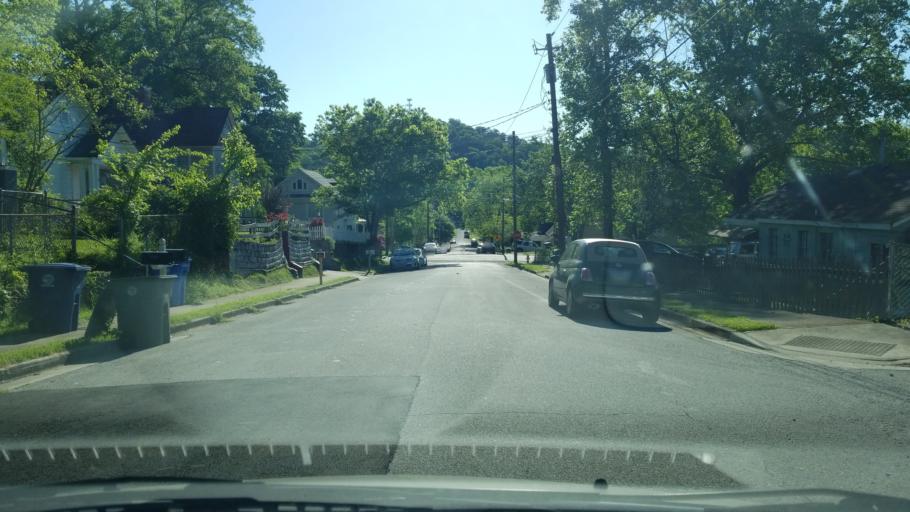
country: US
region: Tennessee
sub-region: Hamilton County
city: Lookout Mountain
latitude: 34.9898
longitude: -85.3319
